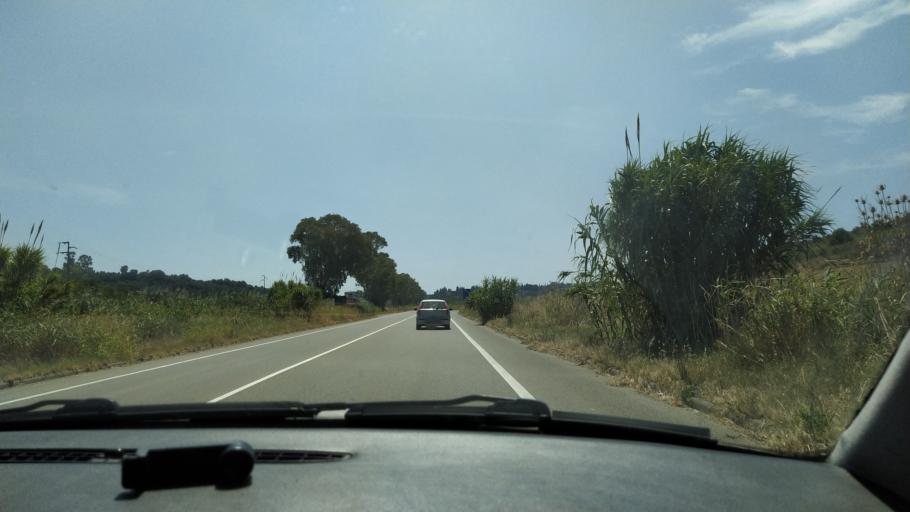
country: IT
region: Apulia
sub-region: Provincia di Taranto
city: Marina di Ginosa
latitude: 40.4410
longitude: 16.7832
